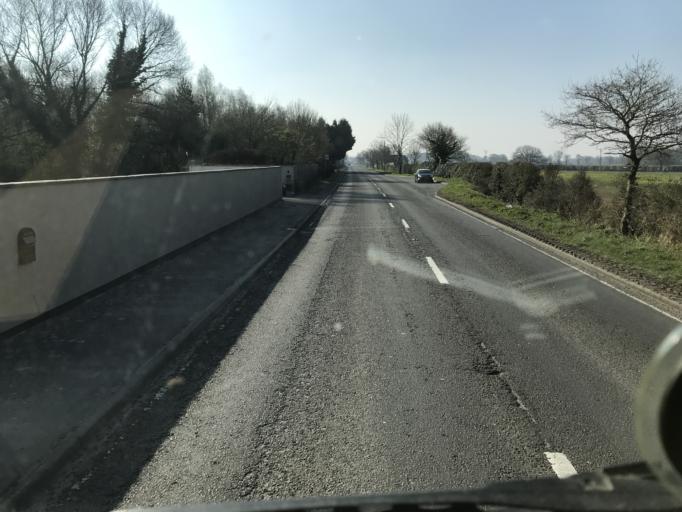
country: GB
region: England
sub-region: Cheshire West and Chester
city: Waverton
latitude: 53.1543
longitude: -2.8123
